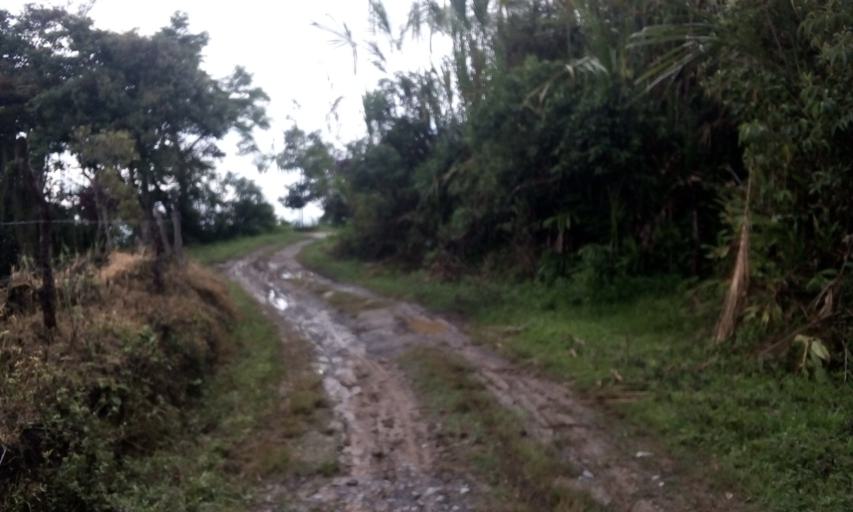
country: CO
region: Boyaca
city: Santana
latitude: 6.0022
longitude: -73.4968
